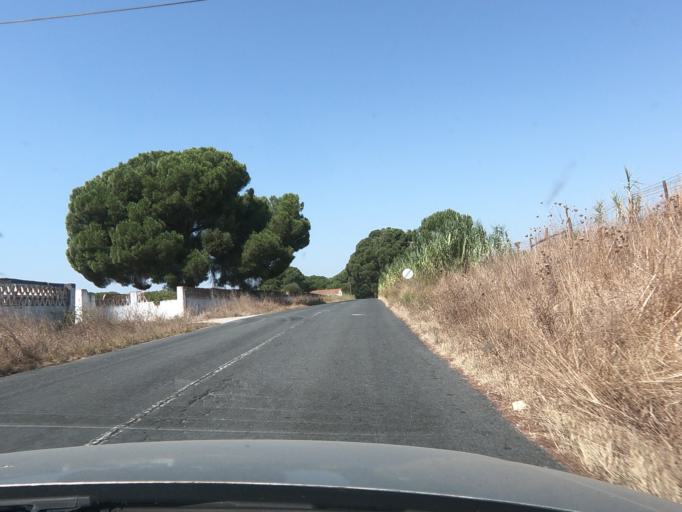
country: PT
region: Setubal
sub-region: Alcacer do Sal
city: Alcacer do Sal
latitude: 38.2787
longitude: -8.3947
